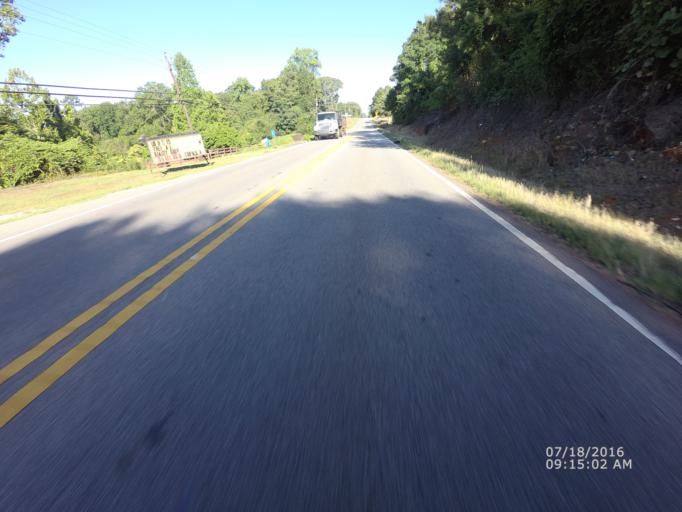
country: US
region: Alabama
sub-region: Chambers County
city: Huguley
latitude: 32.8480
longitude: -85.2484
